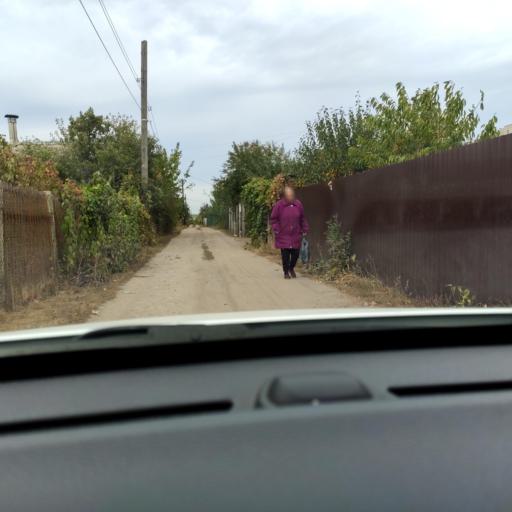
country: RU
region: Voronezj
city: Voronezh
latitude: 51.6689
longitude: 39.2848
